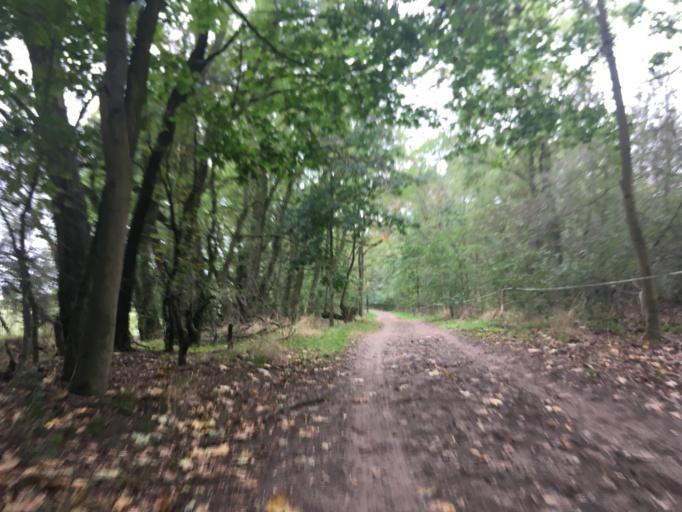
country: DE
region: Brandenburg
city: Falkensee
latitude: 52.5110
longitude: 13.0994
